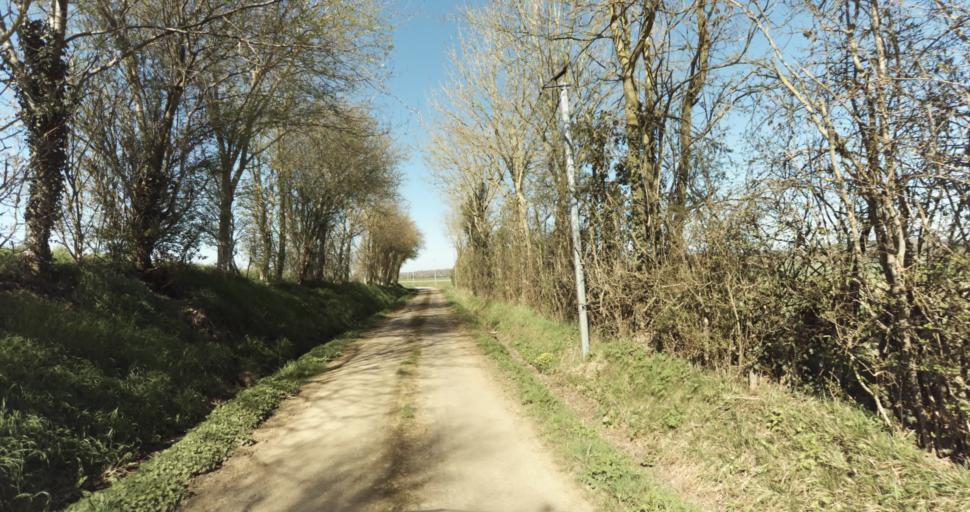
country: FR
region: Lower Normandy
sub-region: Departement du Calvados
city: Saint-Pierre-sur-Dives
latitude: 49.0204
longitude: 0.0141
